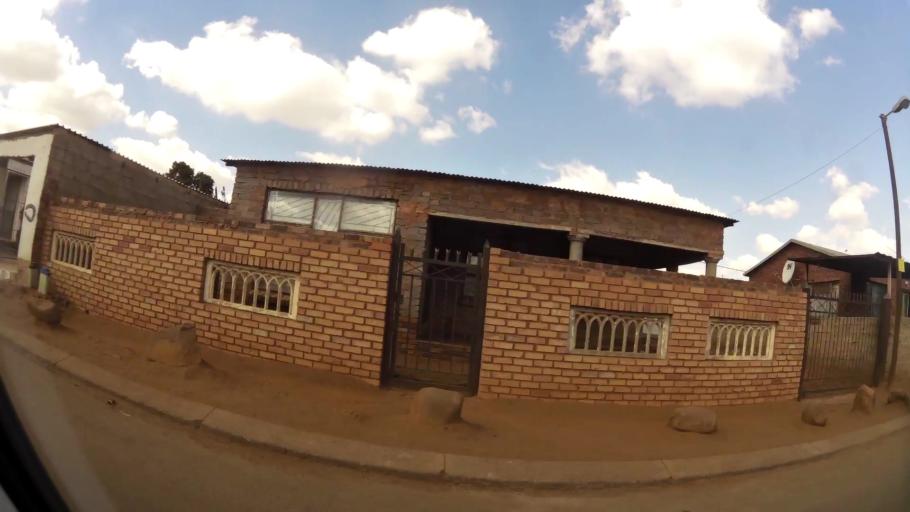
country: ZA
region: Gauteng
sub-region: City of Tshwane Metropolitan Municipality
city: Cullinan
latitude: -25.7028
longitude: 28.4033
